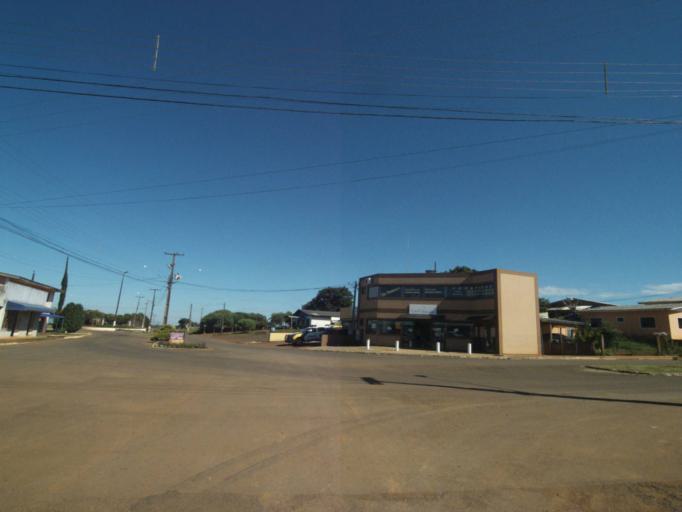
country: BR
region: Parana
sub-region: Pinhao
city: Pinhao
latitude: -25.8343
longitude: -52.0282
